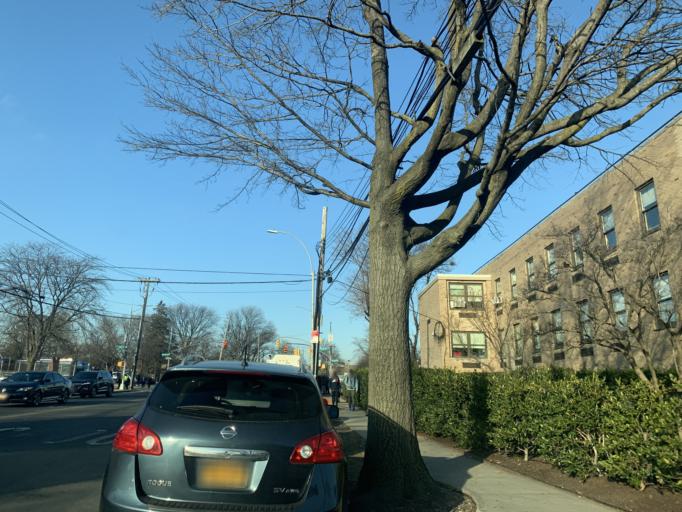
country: US
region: New York
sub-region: Bronx
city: The Bronx
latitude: 40.8565
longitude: -73.8439
